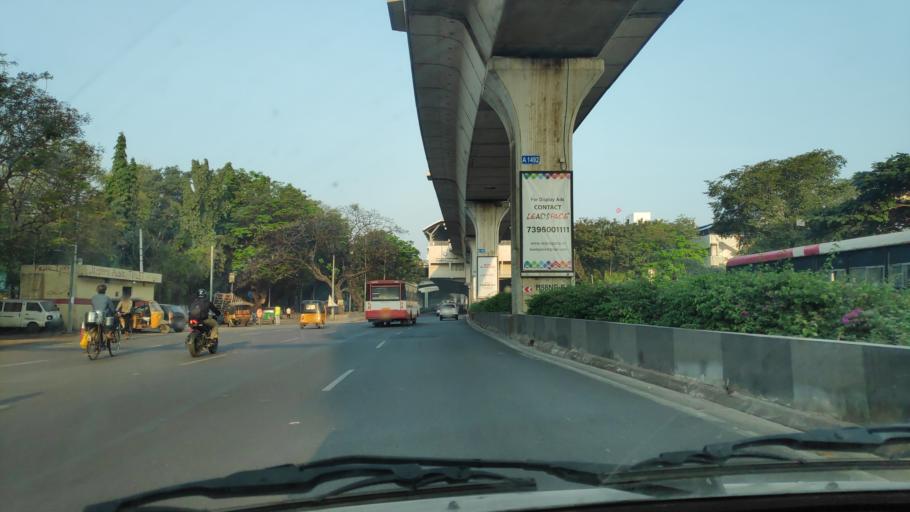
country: IN
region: Telangana
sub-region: Rangareddi
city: Gaddi Annaram
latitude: 17.3702
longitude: 78.5137
